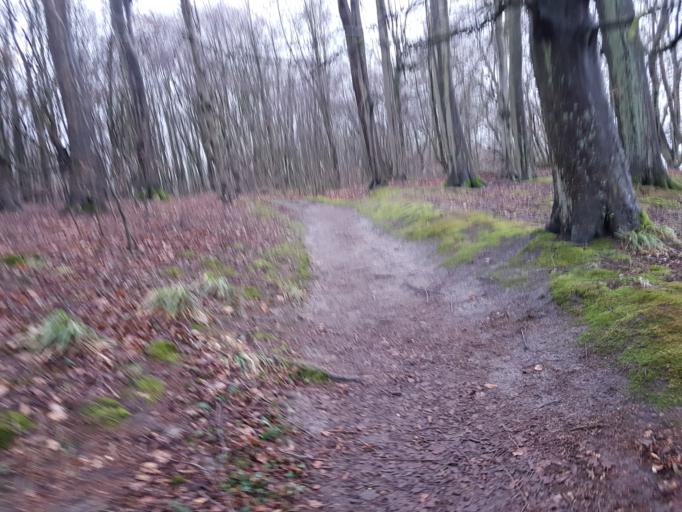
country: DE
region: Mecklenburg-Vorpommern
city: Ostseebad Sellin
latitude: 54.3991
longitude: 13.6604
